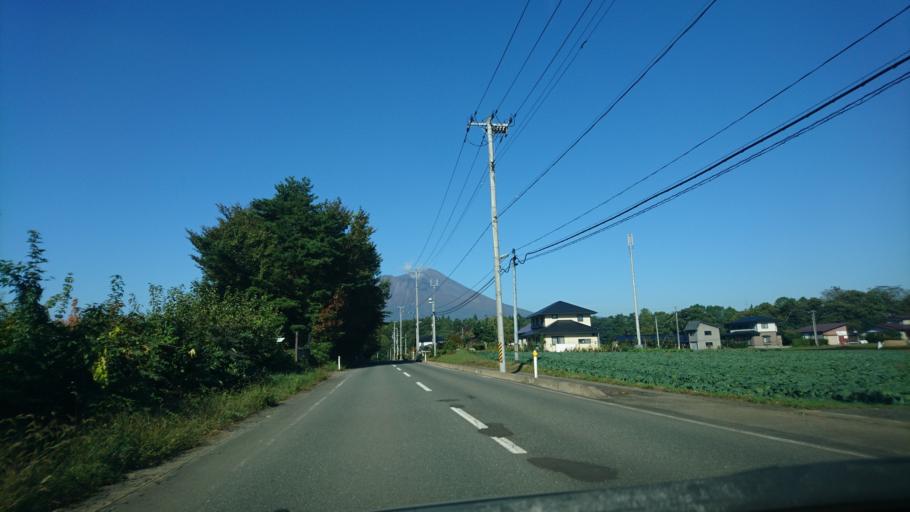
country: JP
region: Iwate
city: Morioka-shi
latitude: 39.8109
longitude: 141.1343
